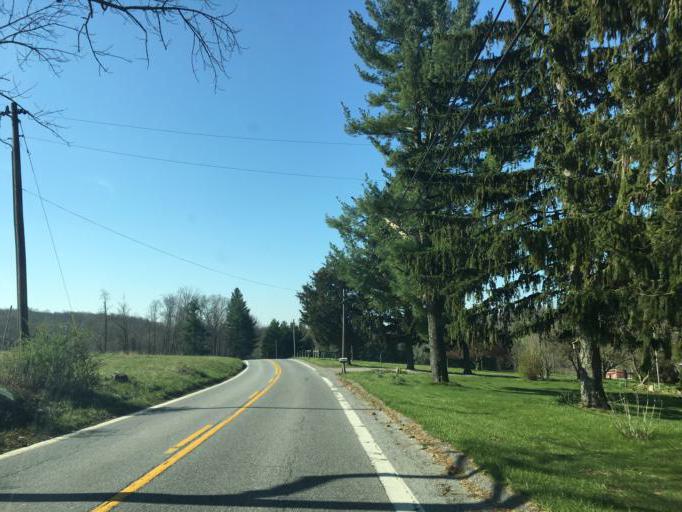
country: US
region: Maryland
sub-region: Washington County
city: Cavetown
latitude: 39.5957
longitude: -77.5586
